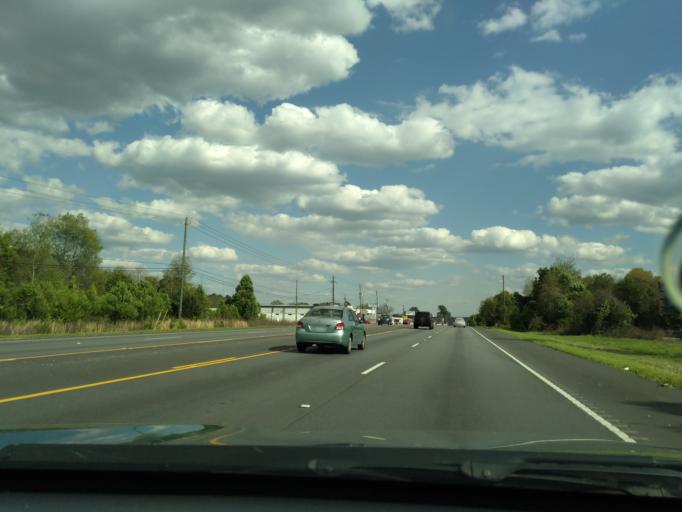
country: US
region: South Carolina
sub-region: Florence County
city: Florence
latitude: 34.2179
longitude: -79.7848
